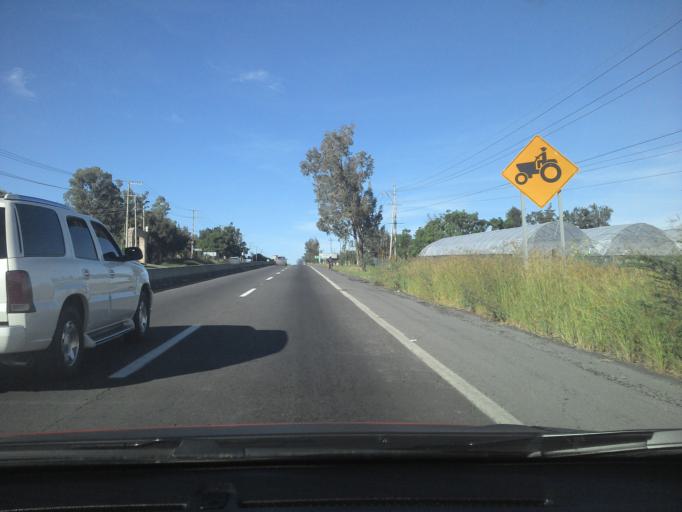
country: MX
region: Jalisco
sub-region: Tala
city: Los Ruisenores
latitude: 20.6962
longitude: -103.6902
